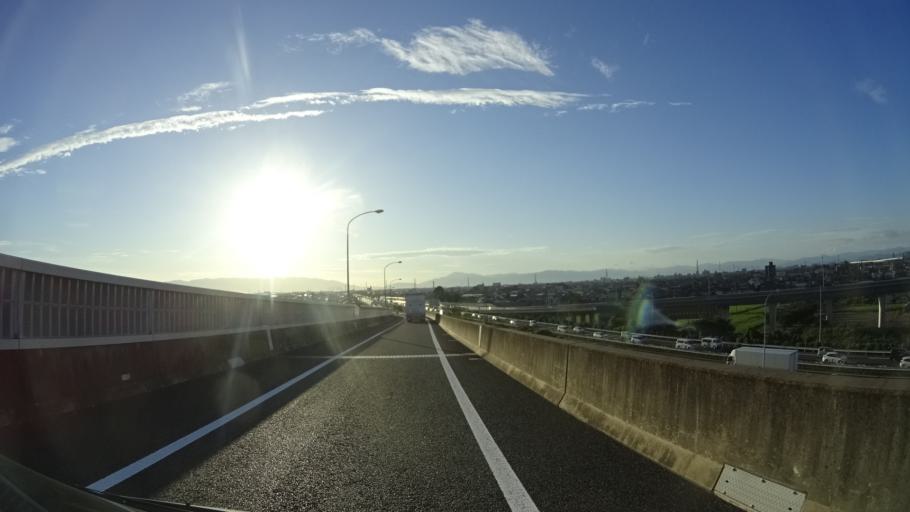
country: JP
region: Aichi
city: Ichinomiya
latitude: 35.2822
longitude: 136.7794
